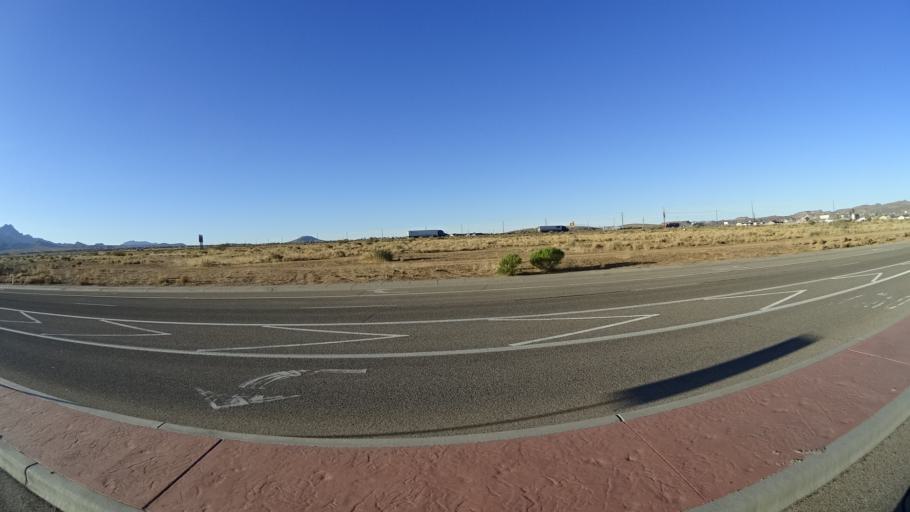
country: US
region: Arizona
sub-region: Mohave County
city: New Kingman-Butler
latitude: 35.2182
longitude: -113.9892
